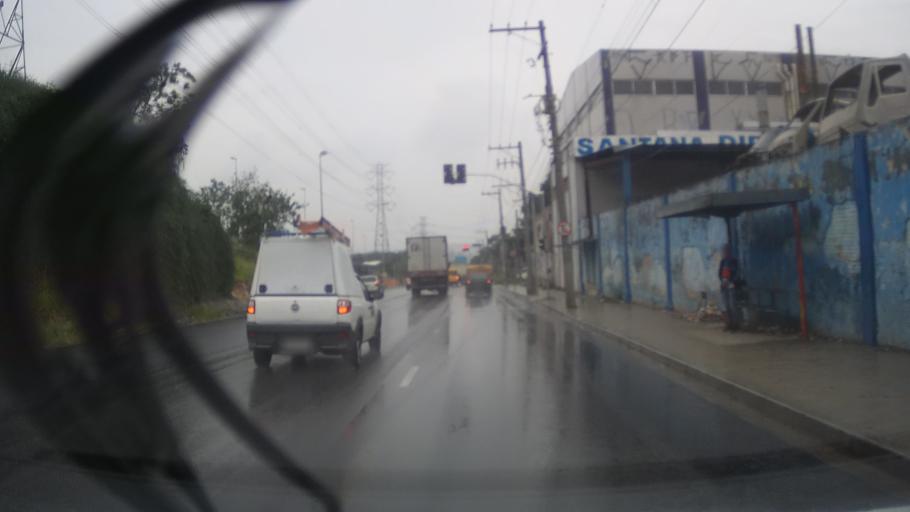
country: BR
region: Sao Paulo
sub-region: Guarulhos
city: Guarulhos
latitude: -23.4637
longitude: -46.4688
